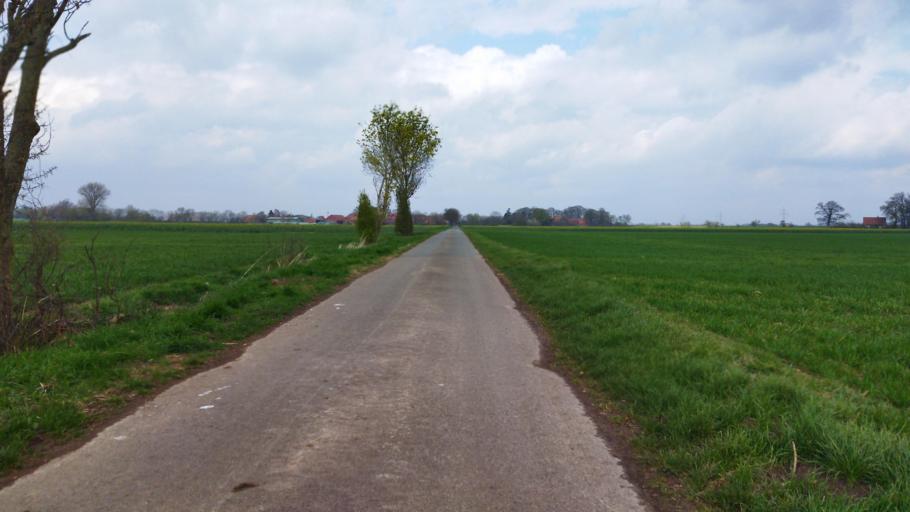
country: DE
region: Lower Saxony
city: Hilgermissen
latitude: 52.8811
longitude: 9.1719
